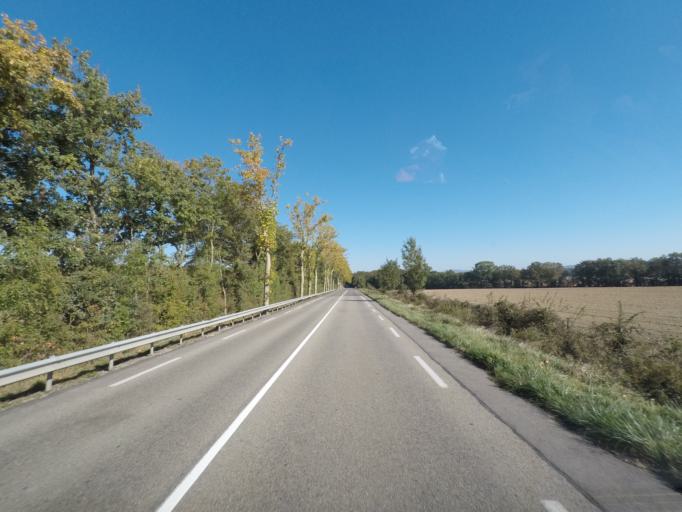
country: FR
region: Rhone-Alpes
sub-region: Departement de l'Ain
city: Servas
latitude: 46.1409
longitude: 5.1715
